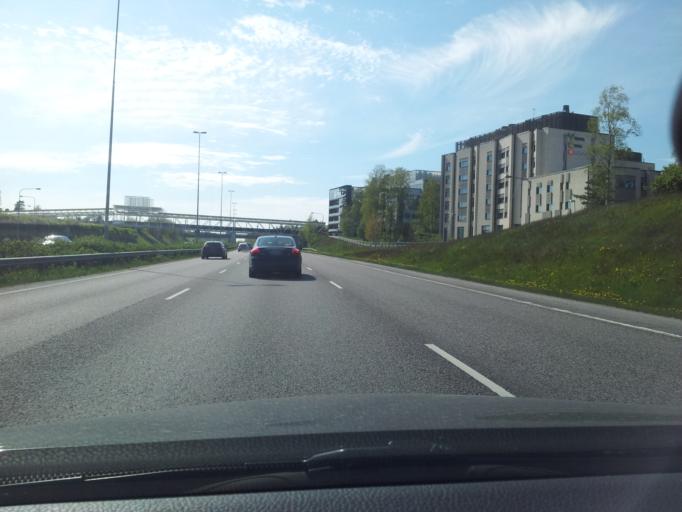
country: FI
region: Uusimaa
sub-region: Helsinki
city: Otaniemi
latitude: 60.1698
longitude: 24.8096
